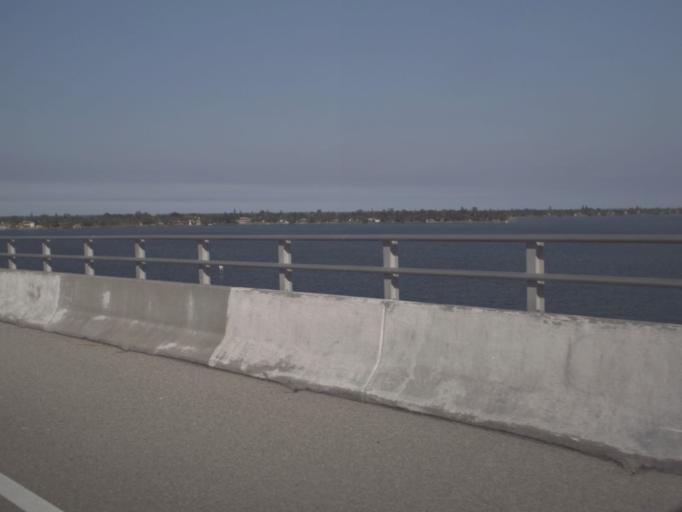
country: US
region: Florida
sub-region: Brevard County
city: Melbourne
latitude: 28.0840
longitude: -80.5912
